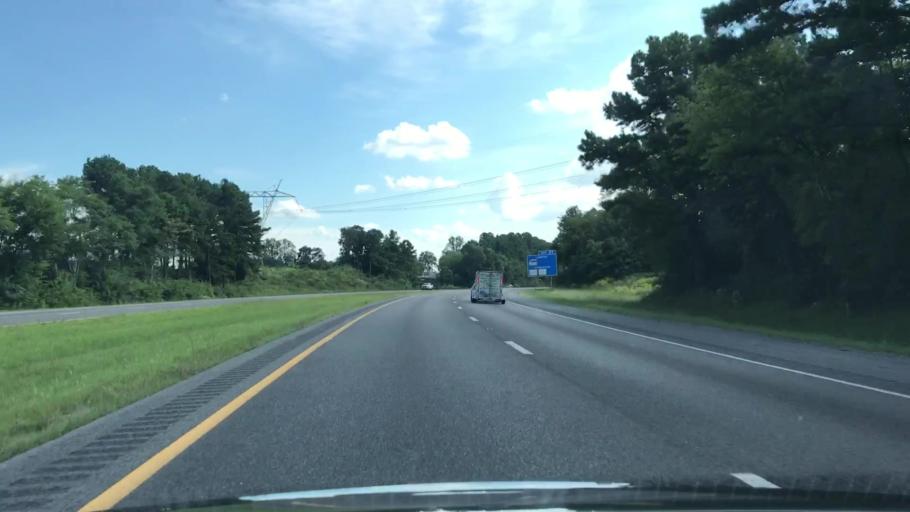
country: US
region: Tennessee
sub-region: Marshall County
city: Cornersville
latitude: 35.3933
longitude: -86.8789
